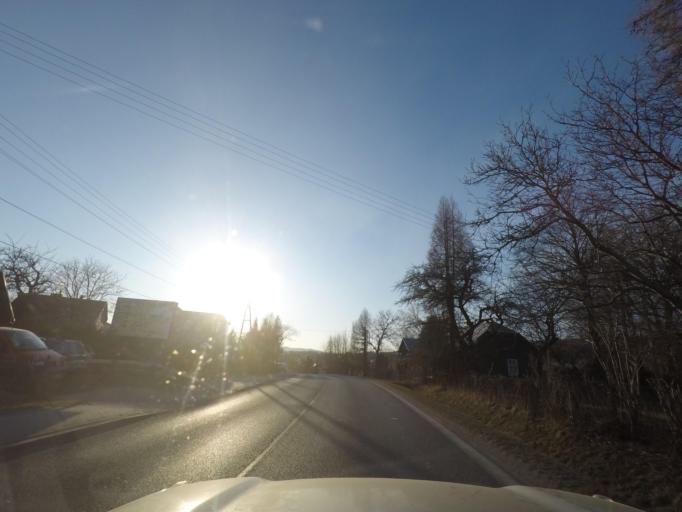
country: PL
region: Subcarpathian Voivodeship
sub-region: Powiat krosnienski
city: Dukla
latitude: 49.5585
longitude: 21.6733
